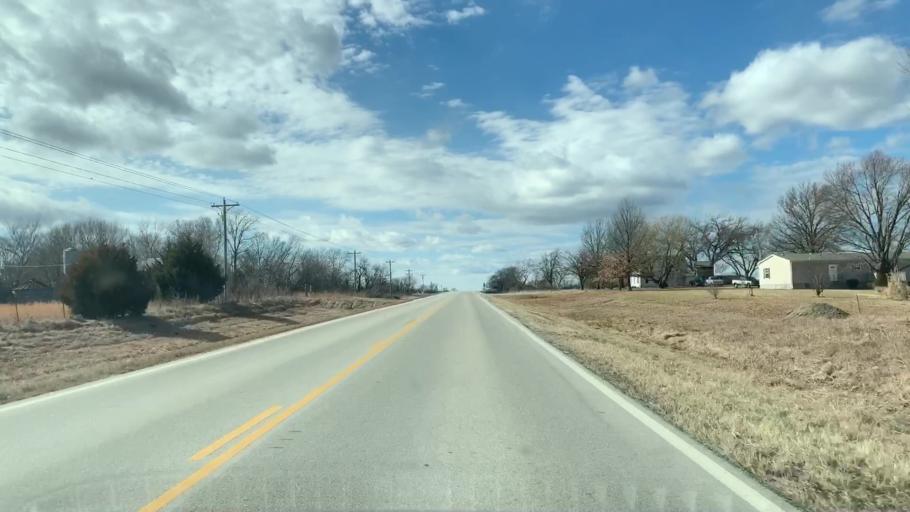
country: US
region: Kansas
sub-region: Neosho County
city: Erie
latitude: 37.5292
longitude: -95.2767
